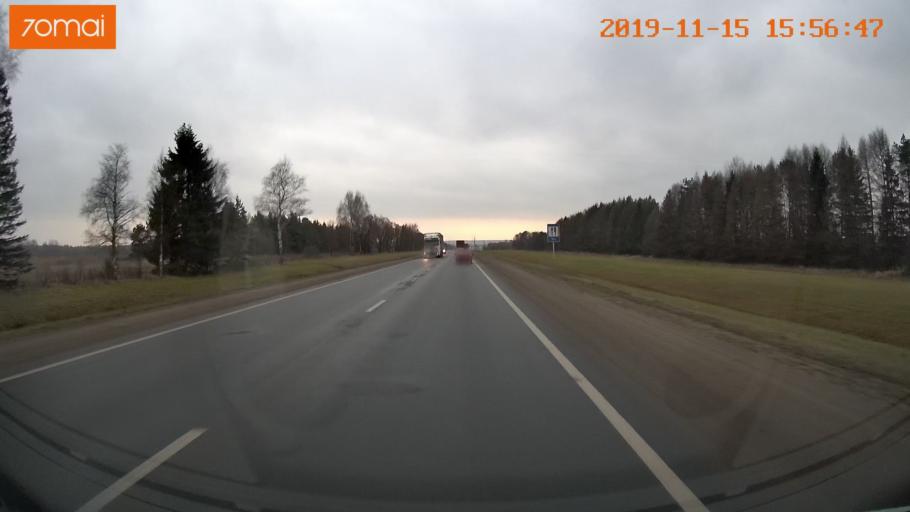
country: RU
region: Jaroslavl
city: Yaroslavl
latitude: 57.8380
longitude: 39.9698
